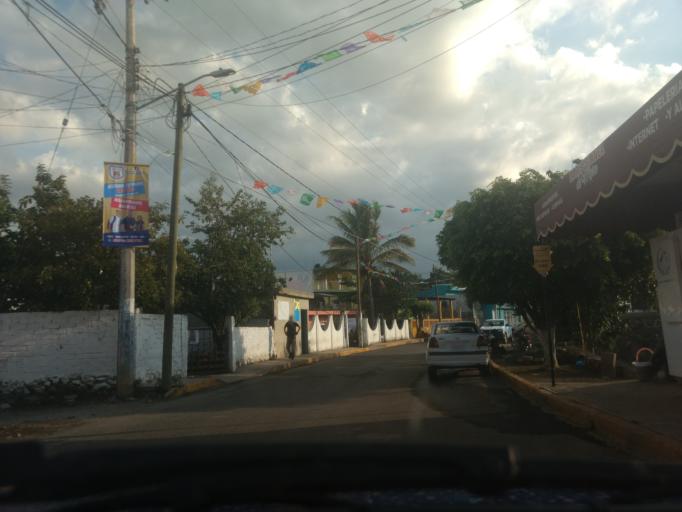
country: MX
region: Nayarit
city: Puga
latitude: 21.5261
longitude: -104.8075
